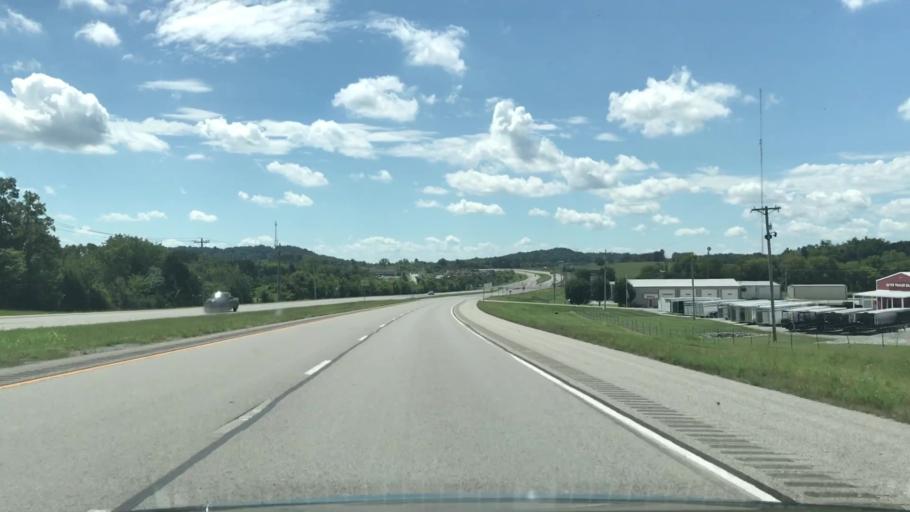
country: US
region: Kentucky
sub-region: Logan County
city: Russellville
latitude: 36.8527
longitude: -86.9185
